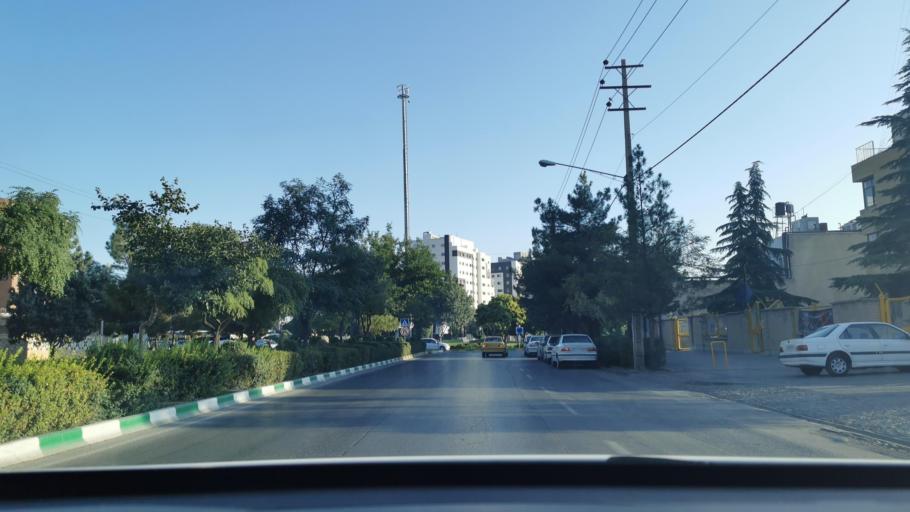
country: IR
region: Razavi Khorasan
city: Mashhad
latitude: 36.3582
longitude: 59.5130
